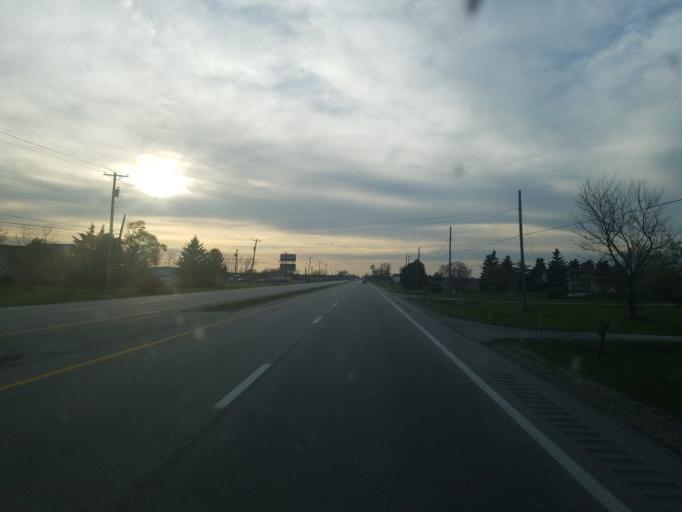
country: US
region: Ohio
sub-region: Sandusky County
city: Gibsonburg
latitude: 41.4156
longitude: -83.2769
